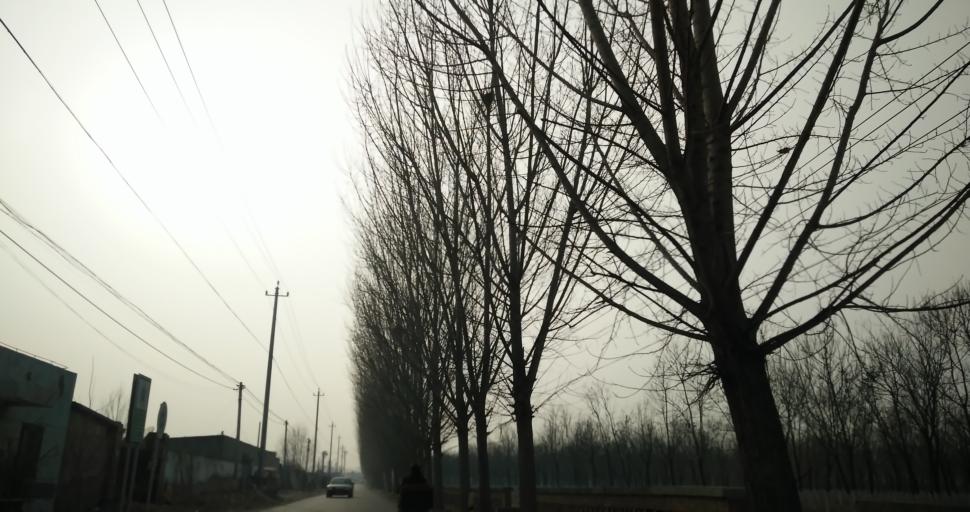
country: CN
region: Beijing
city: Xingfeng
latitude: 39.7123
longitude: 116.3646
